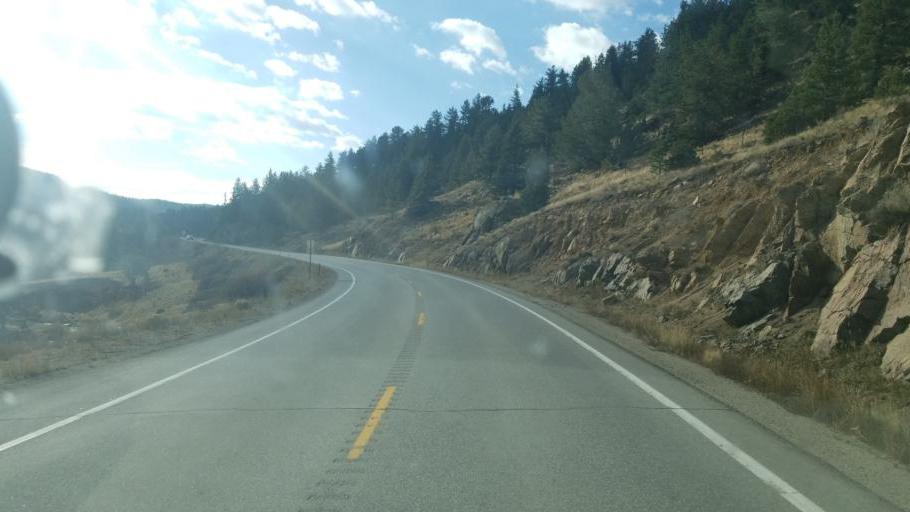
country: US
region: Colorado
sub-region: Chaffee County
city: Buena Vista
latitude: 38.8565
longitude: -105.9860
